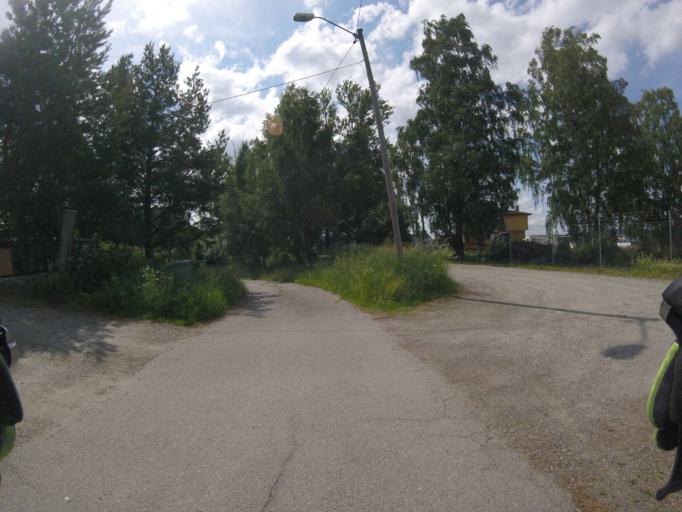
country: NO
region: Akershus
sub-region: Skedsmo
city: Lillestrom
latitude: 59.9740
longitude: 11.0550
